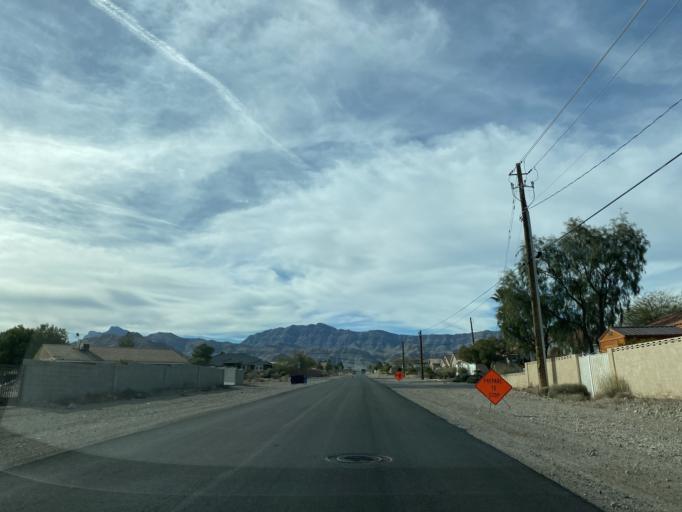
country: US
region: Nevada
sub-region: Clark County
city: Summerlin South
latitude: 36.2700
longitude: -115.3161
